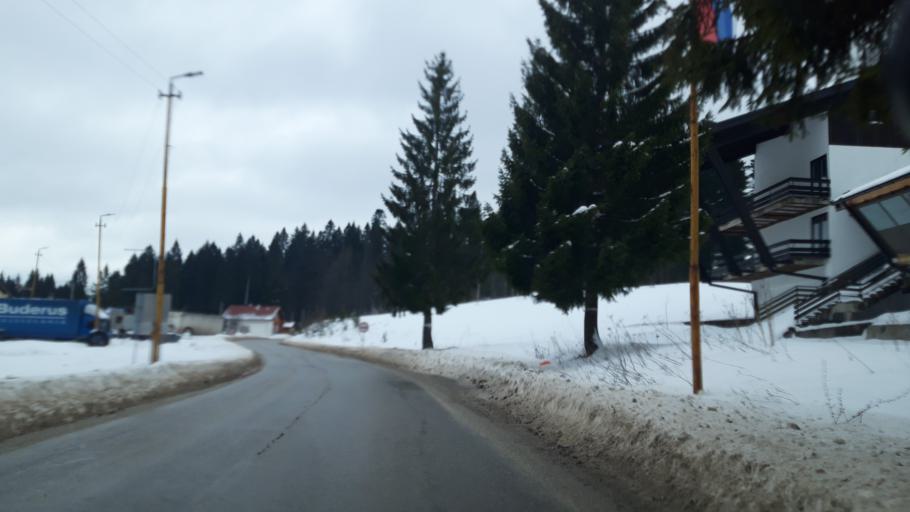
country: BA
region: Republika Srpska
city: Han Pijesak
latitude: 44.0801
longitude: 18.9522
